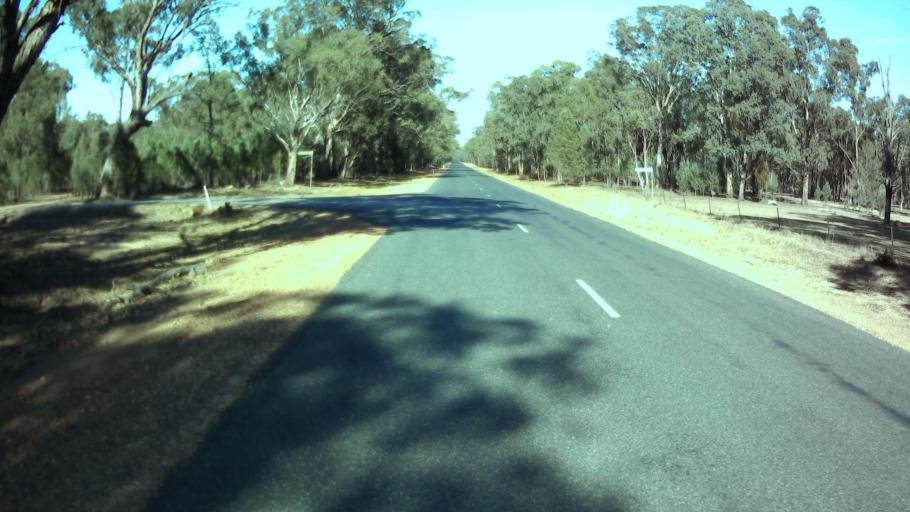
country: AU
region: New South Wales
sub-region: Weddin
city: Grenfell
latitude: -34.0245
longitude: 148.0159
